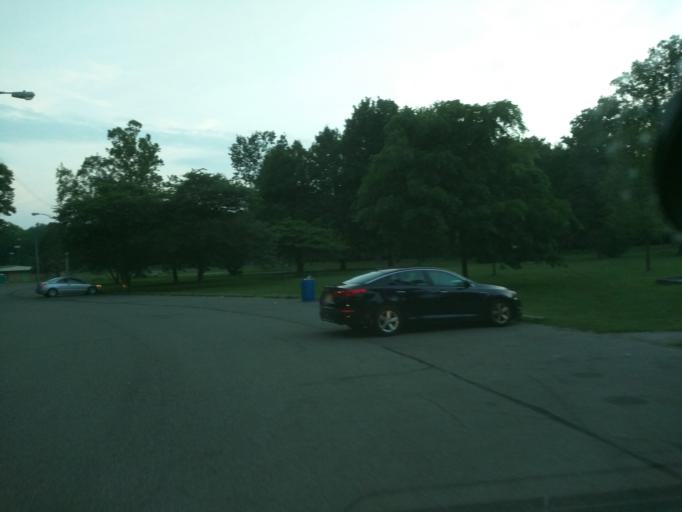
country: US
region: Michigan
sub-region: Ingham County
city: Lansing
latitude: 42.7058
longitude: -84.5595
